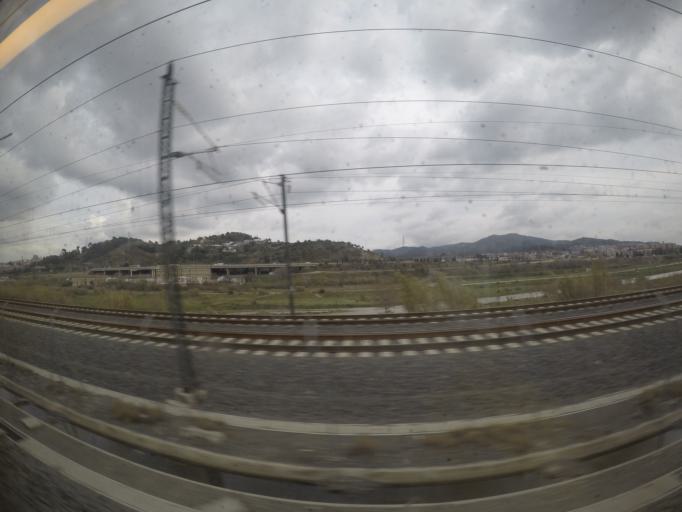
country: ES
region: Catalonia
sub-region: Provincia de Barcelona
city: Palleja
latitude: 41.4210
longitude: 2.0041
